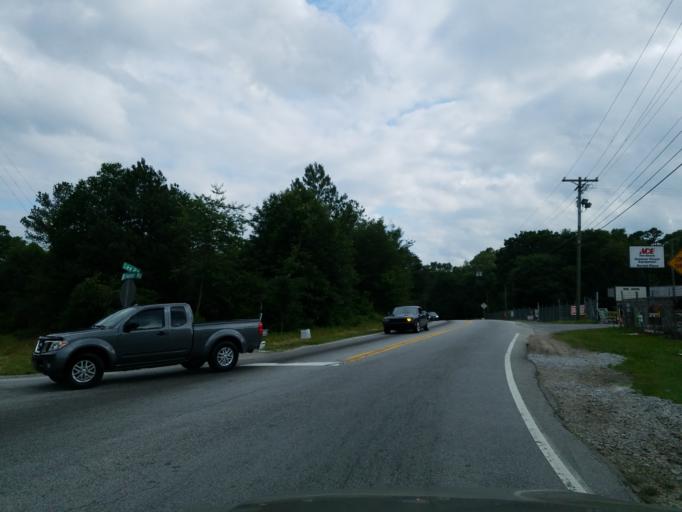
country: US
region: Georgia
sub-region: Douglas County
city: Lithia Springs
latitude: 33.7773
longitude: -84.6529
